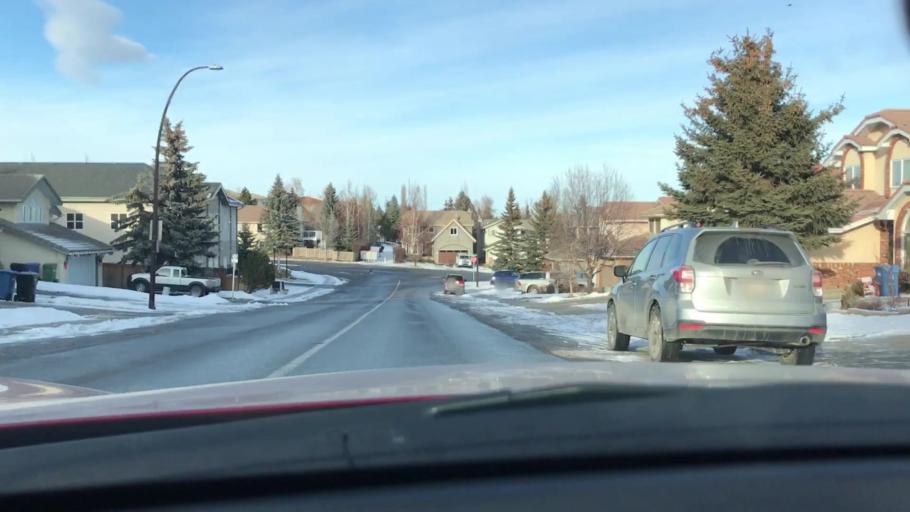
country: CA
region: Alberta
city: Calgary
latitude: 51.0316
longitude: -114.1703
